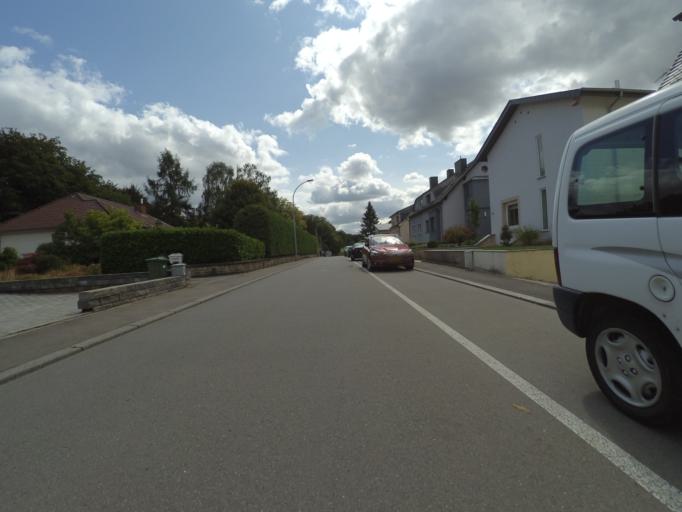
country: LU
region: Luxembourg
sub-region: Canton de Luxembourg
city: Niederanven
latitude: 49.6491
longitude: 6.2268
